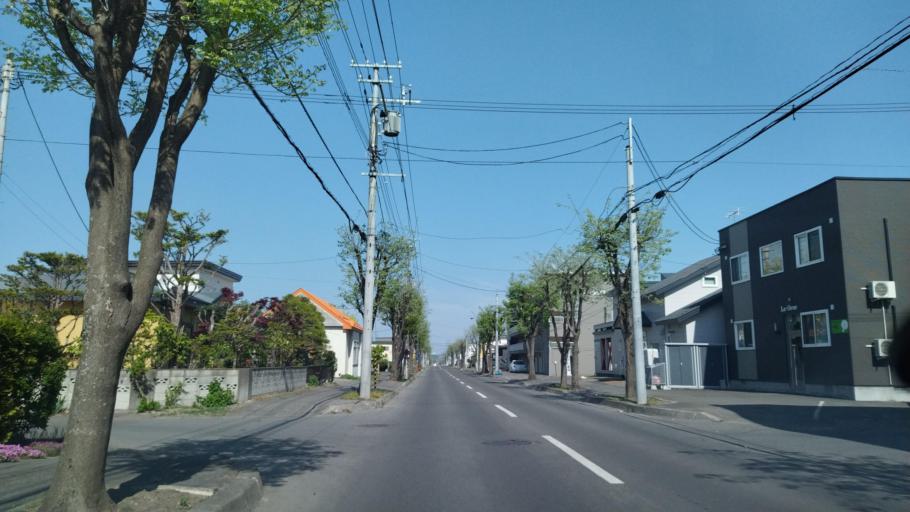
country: JP
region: Hokkaido
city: Obihiro
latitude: 42.8958
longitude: 143.1886
